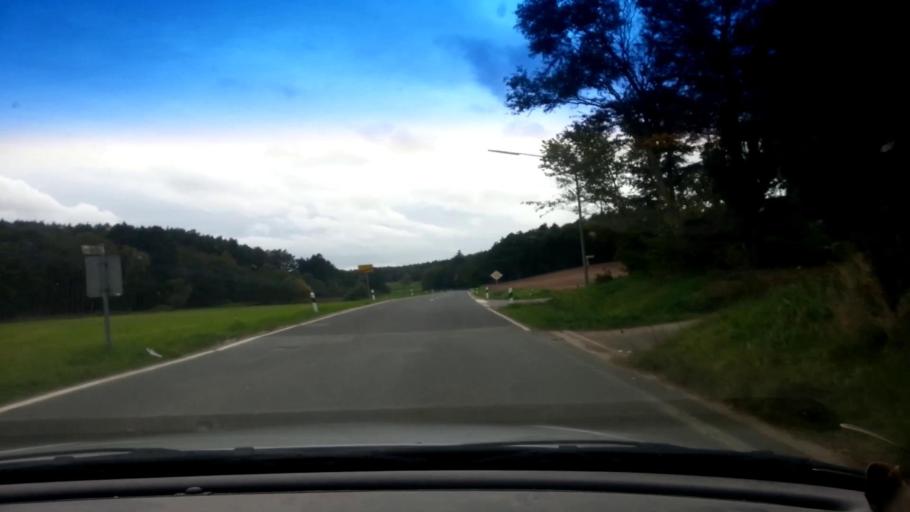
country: DE
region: Bavaria
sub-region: Upper Franconia
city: Gerach
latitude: 50.0405
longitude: 10.7866
